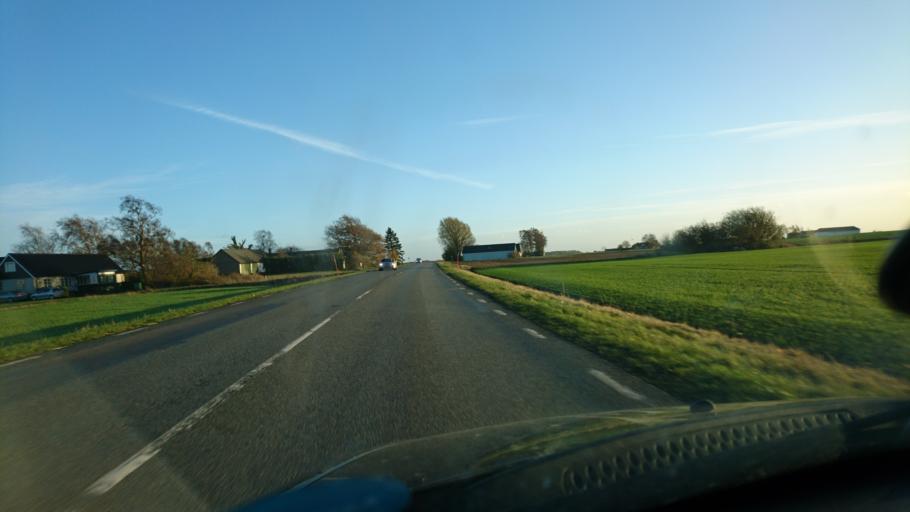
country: SE
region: Skane
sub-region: Simrishamns Kommun
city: Simrishamn
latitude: 55.4874
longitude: 14.1675
